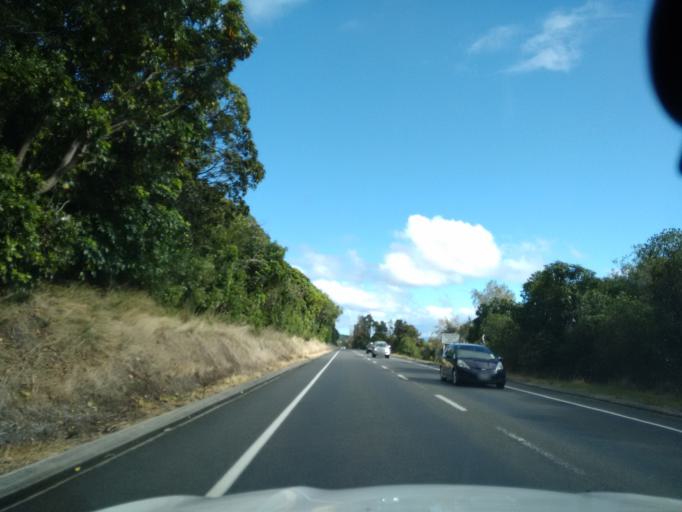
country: NZ
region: Waikato
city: Turangi
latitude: -38.8894
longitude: 175.9514
